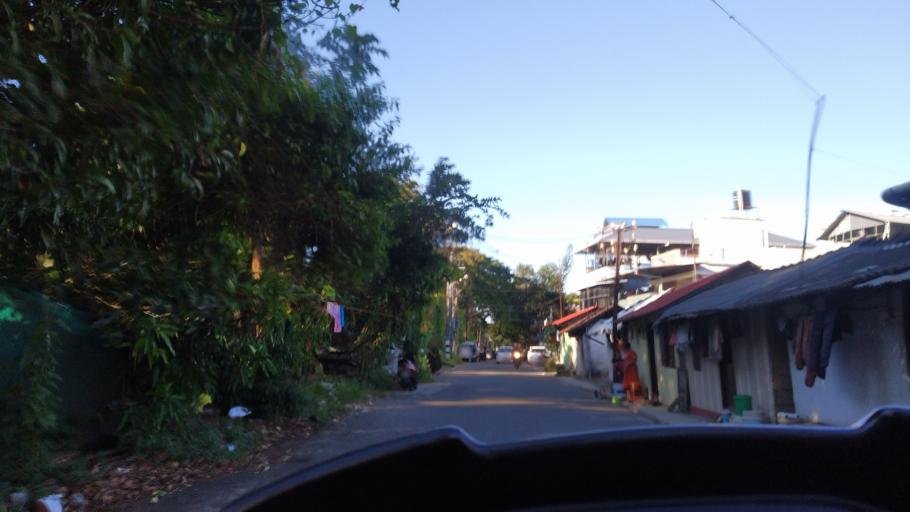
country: IN
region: Kerala
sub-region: Ernakulam
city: Cochin
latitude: 9.9965
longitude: 76.2779
